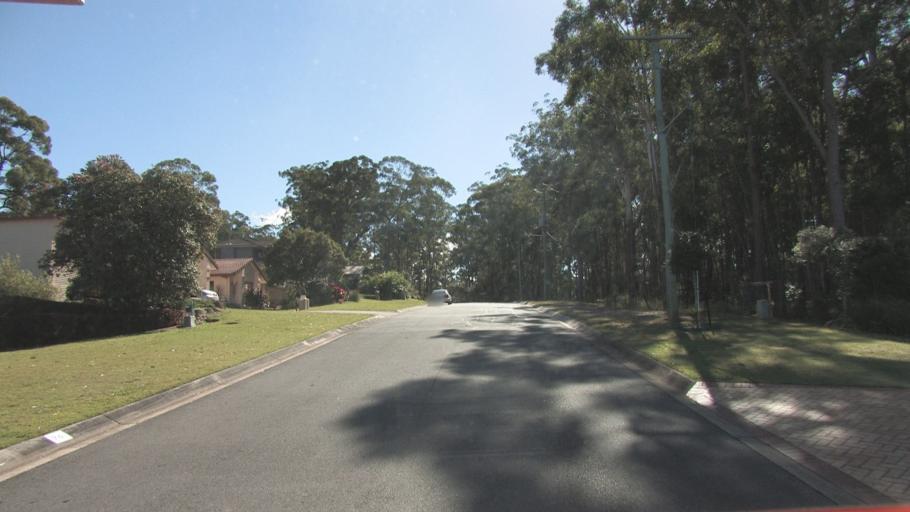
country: AU
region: Queensland
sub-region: Logan
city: Slacks Creek
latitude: -27.6408
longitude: 153.1875
